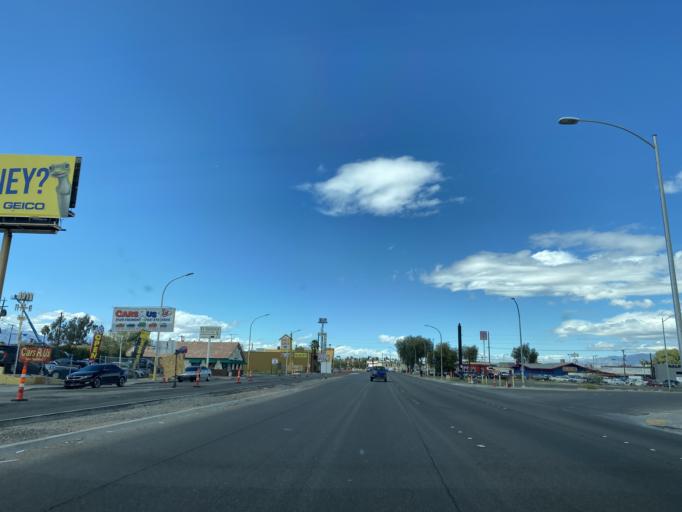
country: US
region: Nevada
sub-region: Clark County
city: Winchester
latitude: 36.1569
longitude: -115.1142
